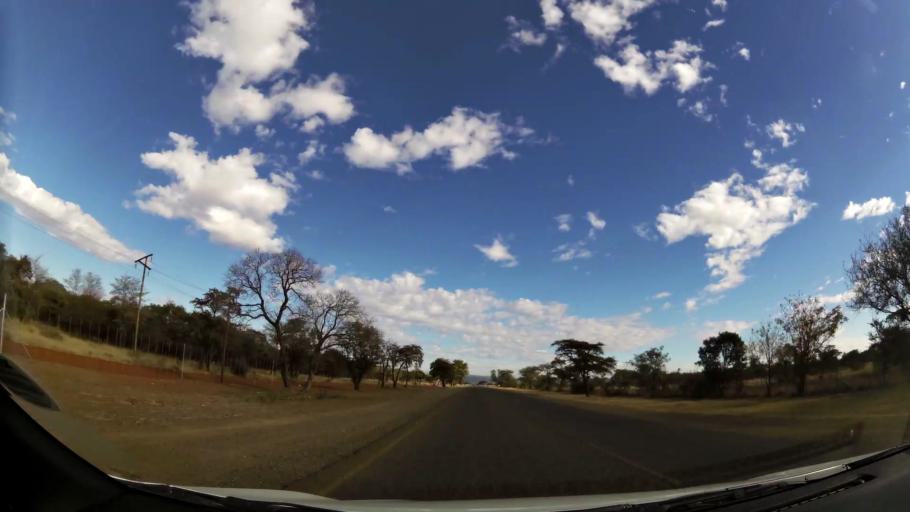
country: ZA
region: Limpopo
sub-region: Waterberg District Municipality
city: Bela-Bela
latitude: -24.9065
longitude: 28.3431
